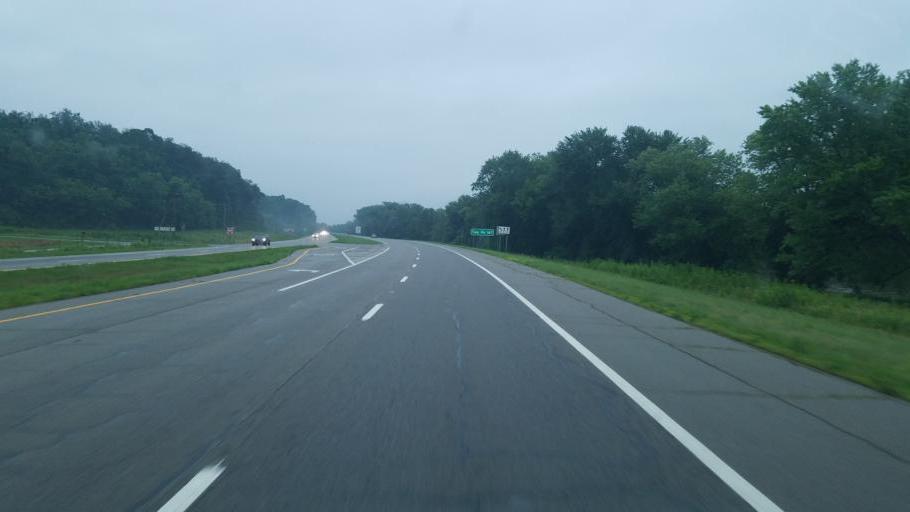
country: US
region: Ohio
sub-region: Coshocton County
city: West Lafayette
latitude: 40.2900
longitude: -81.7379
